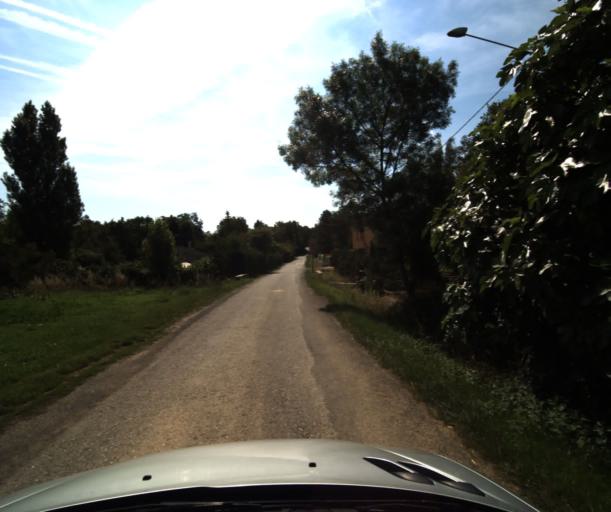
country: FR
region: Midi-Pyrenees
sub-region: Departement de la Haute-Garonne
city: Labastidette
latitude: 43.4696
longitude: 1.2076
